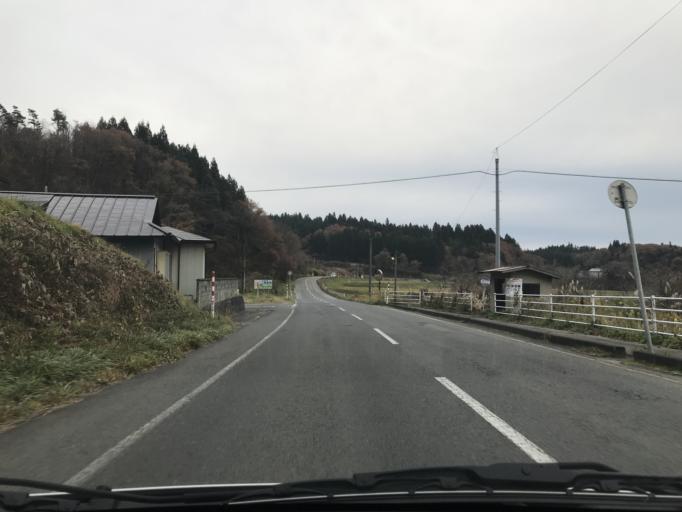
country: JP
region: Iwate
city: Kitakami
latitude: 39.2649
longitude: 141.2682
